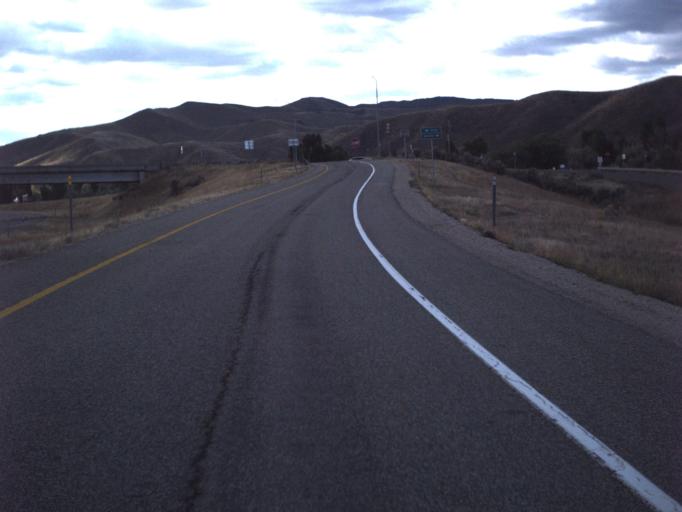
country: US
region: Utah
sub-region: Summit County
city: Coalville
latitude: 41.0175
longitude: -111.4914
